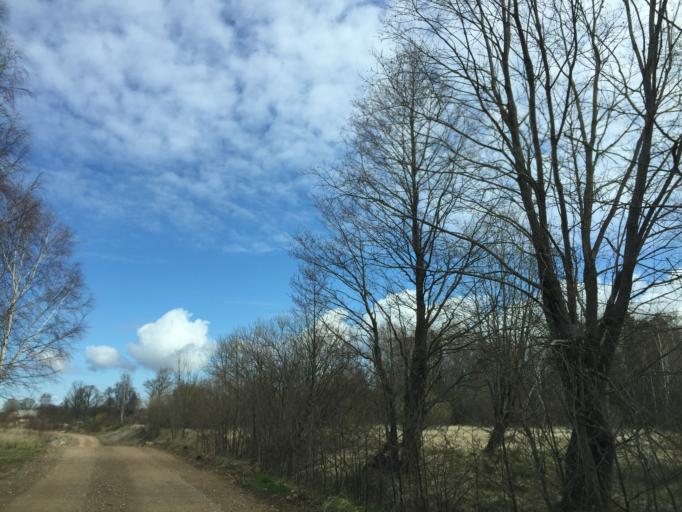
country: LV
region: Salacgrivas
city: Salacgriva
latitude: 57.6034
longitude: 24.3770
